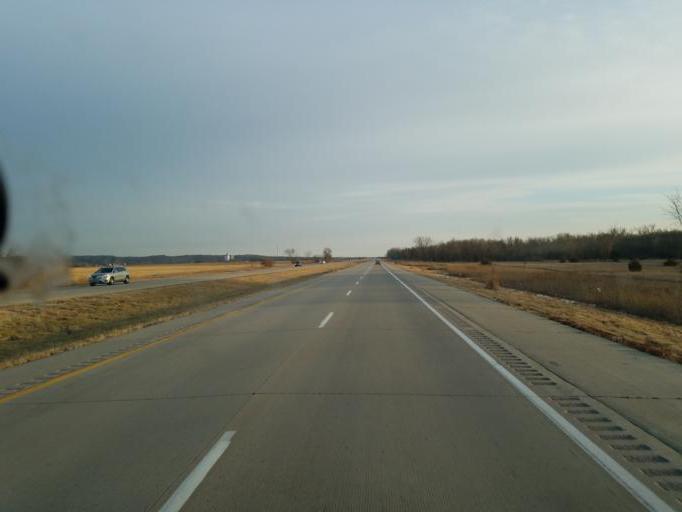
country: US
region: Nebraska
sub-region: Burt County
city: Tekamah
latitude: 41.8200
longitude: -96.0720
